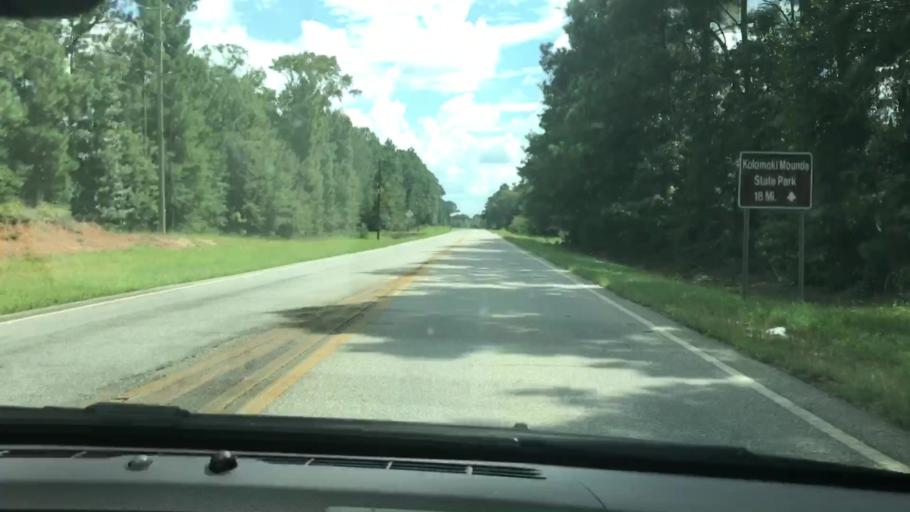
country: US
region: Georgia
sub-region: Clay County
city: Fort Gaines
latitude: 31.6608
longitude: -85.0473
